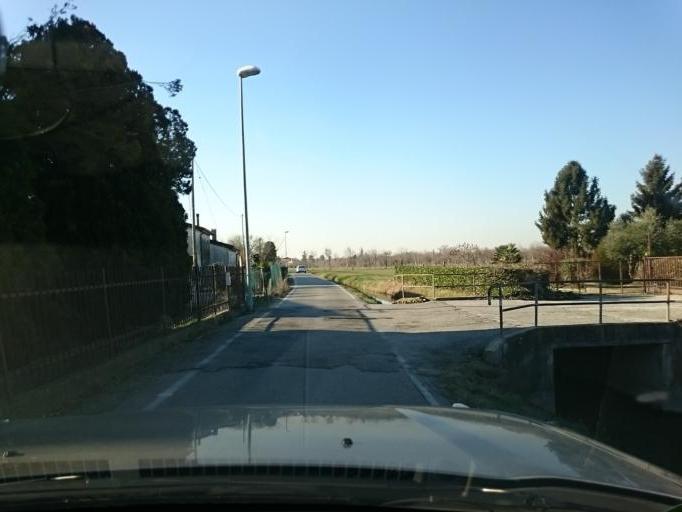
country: IT
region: Veneto
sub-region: Provincia di Venezia
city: Dolo
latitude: 45.4214
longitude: 12.0935
